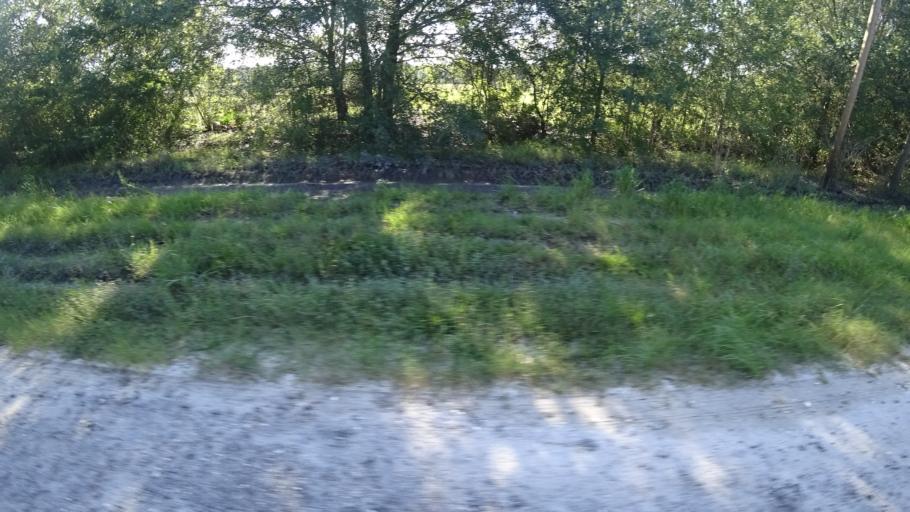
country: US
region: Florida
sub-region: Sarasota County
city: Lake Sarasota
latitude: 27.4134
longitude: -82.2520
